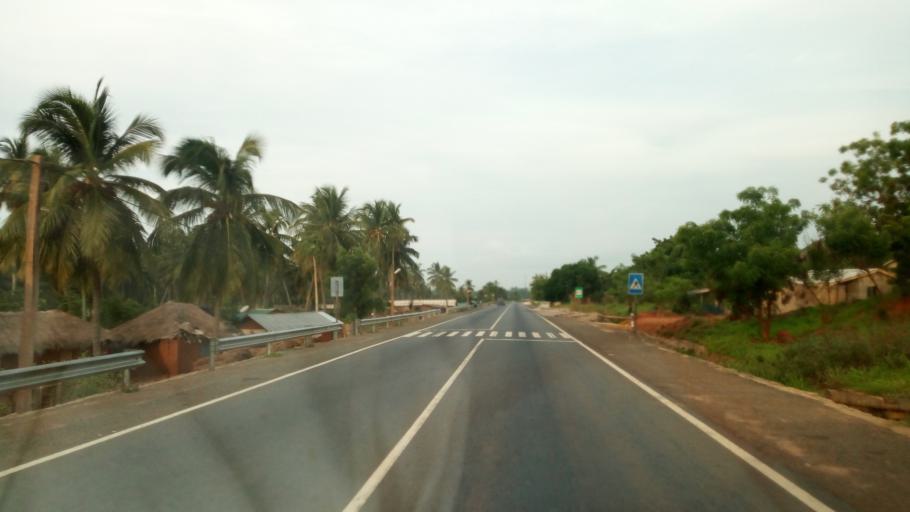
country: TG
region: Maritime
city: Lome
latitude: 6.1013
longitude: 1.0997
